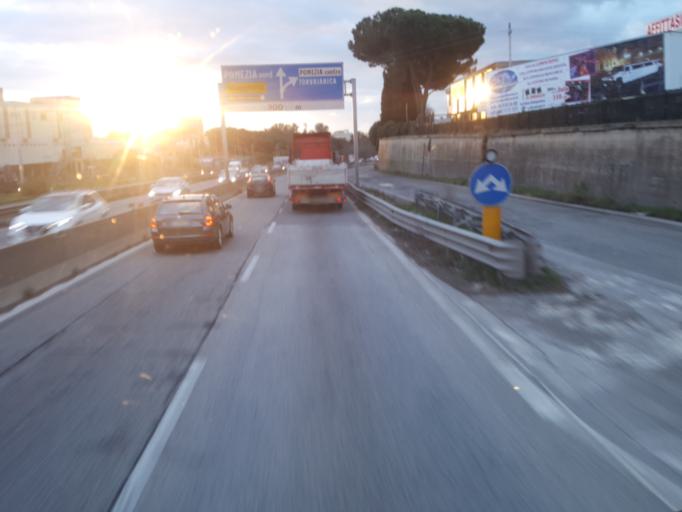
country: IT
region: Latium
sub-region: Citta metropolitana di Roma Capitale
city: Area Produttiva
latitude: 41.6860
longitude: 12.4898
